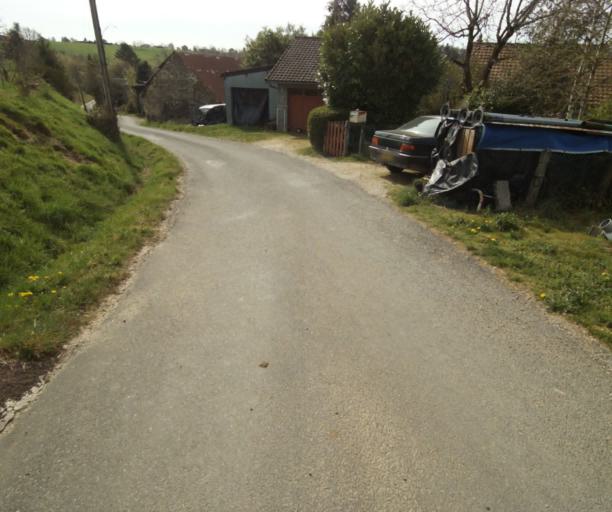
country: FR
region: Limousin
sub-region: Departement de la Correze
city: Correze
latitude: 45.3942
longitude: 1.8056
